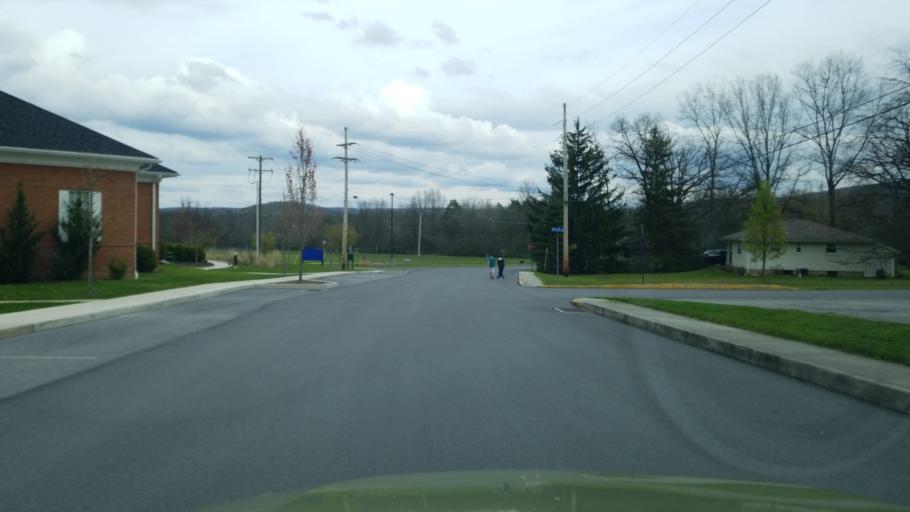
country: US
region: Pennsylvania
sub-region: Blair County
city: Hollidaysburg
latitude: 40.4405
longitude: -78.4021
